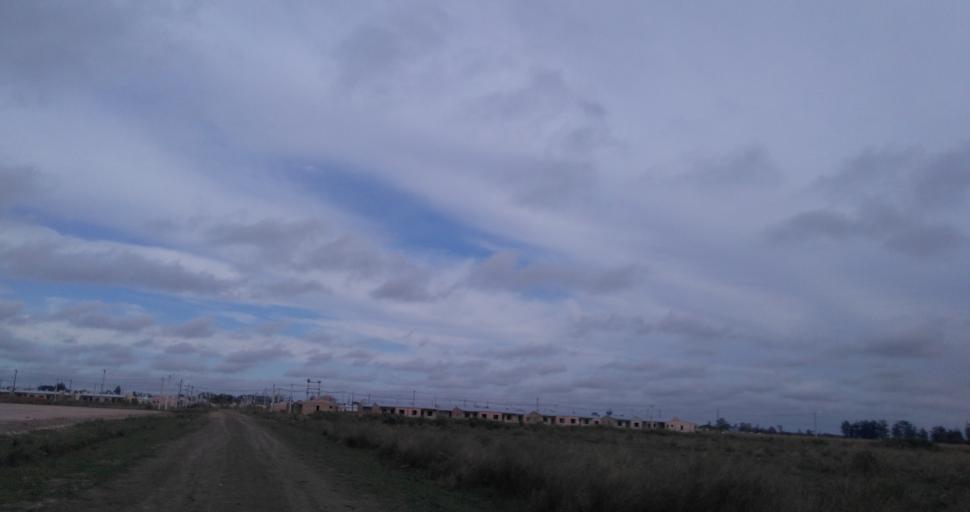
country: AR
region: Chaco
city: Fontana
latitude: -27.3929
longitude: -58.9860
